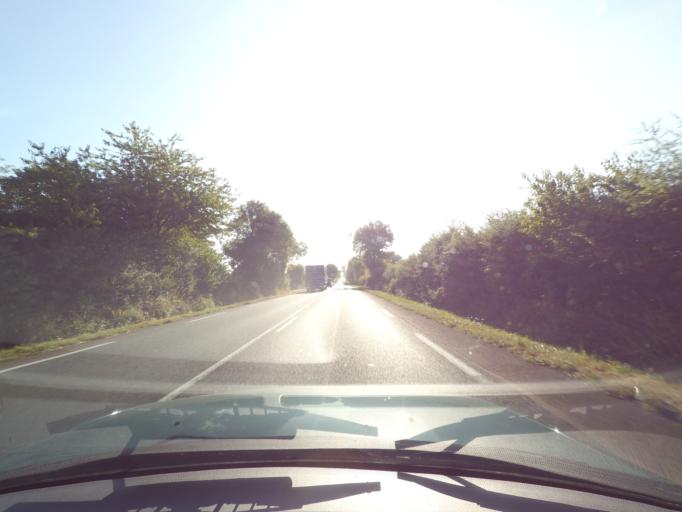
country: FR
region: Poitou-Charentes
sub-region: Departement des Deux-Sevres
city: La Peyratte
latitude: 46.6491
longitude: -0.1804
